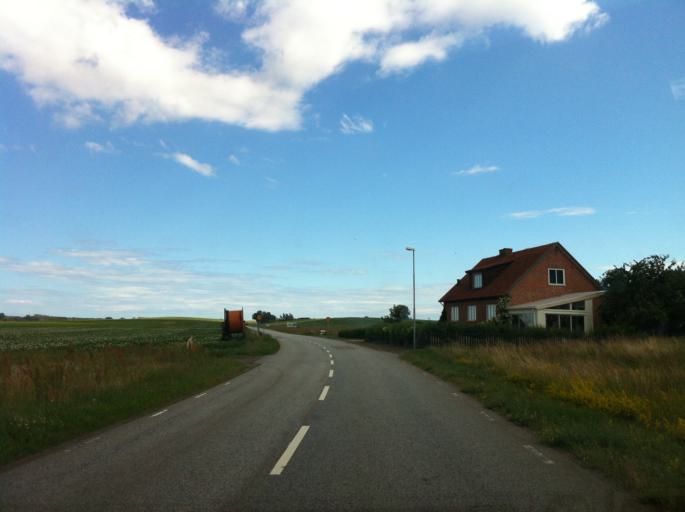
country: SE
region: Skane
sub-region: Ystads Kommun
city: Kopingebro
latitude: 55.4287
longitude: 13.9811
